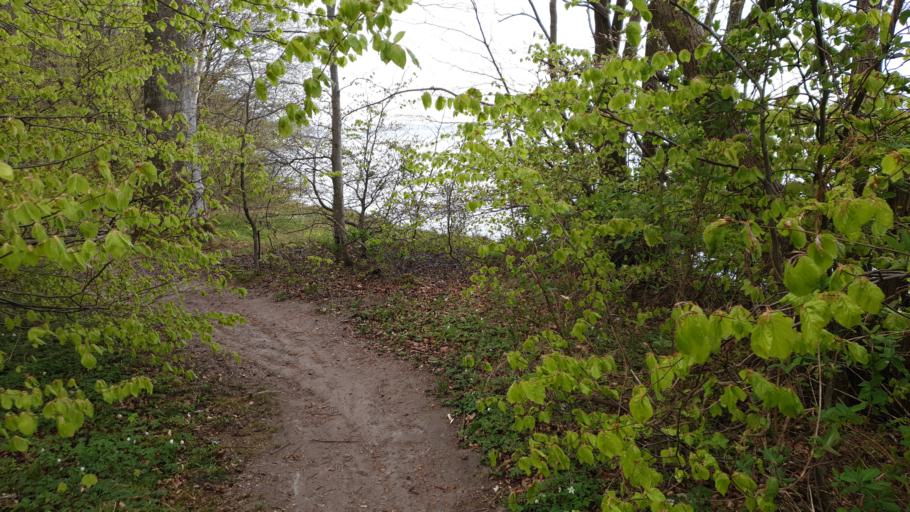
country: DK
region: South Denmark
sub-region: Sonderborg Kommune
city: Dybbol
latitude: 54.8521
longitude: 9.7599
